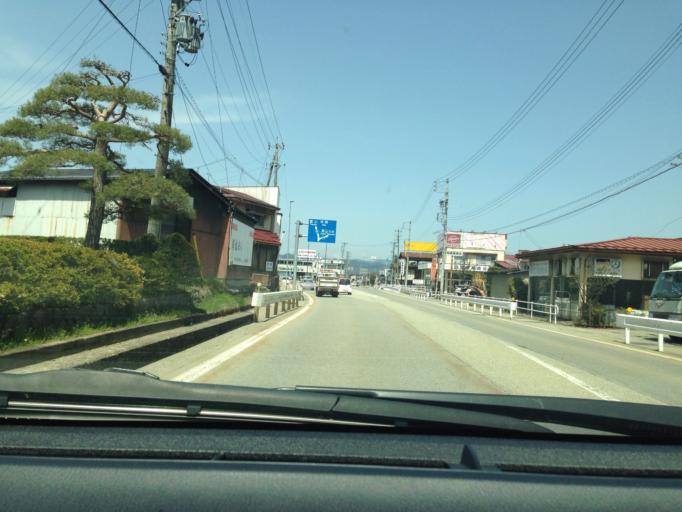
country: JP
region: Gifu
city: Takayama
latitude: 36.1198
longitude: 137.2624
